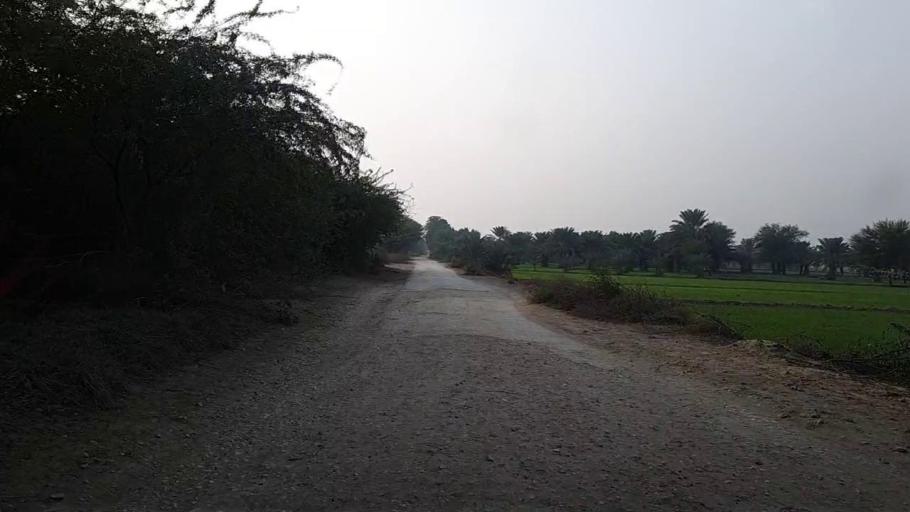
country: PK
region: Sindh
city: Setharja Old
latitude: 27.0811
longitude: 68.5237
